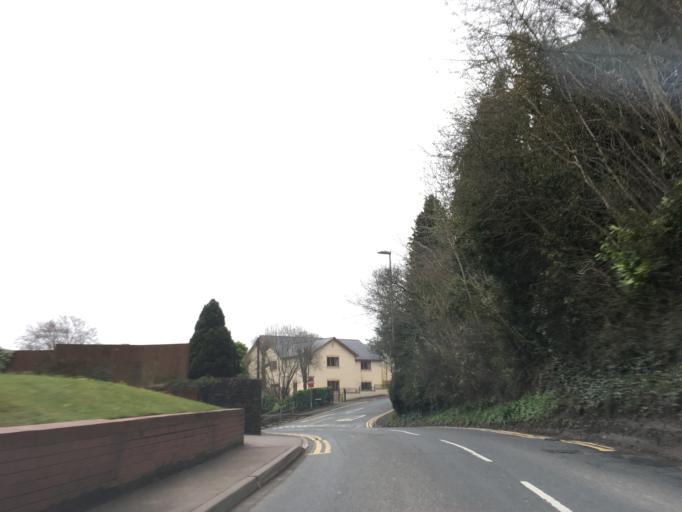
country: GB
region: Wales
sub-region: Newport
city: Caerleon
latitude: 51.6156
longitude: -2.9593
